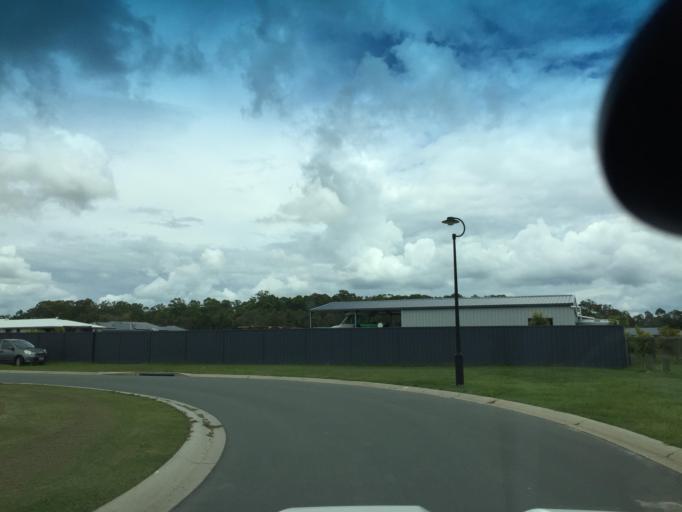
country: AU
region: Queensland
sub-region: Moreton Bay
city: Caboolture
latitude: -27.0412
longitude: 152.9285
